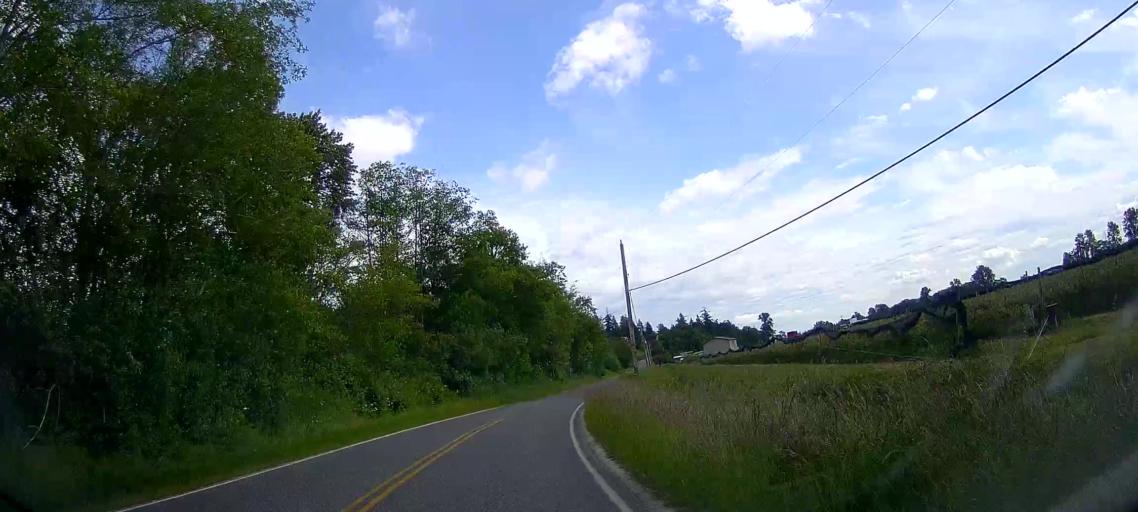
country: US
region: Washington
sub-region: Skagit County
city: Burlington
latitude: 48.5814
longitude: -122.4030
